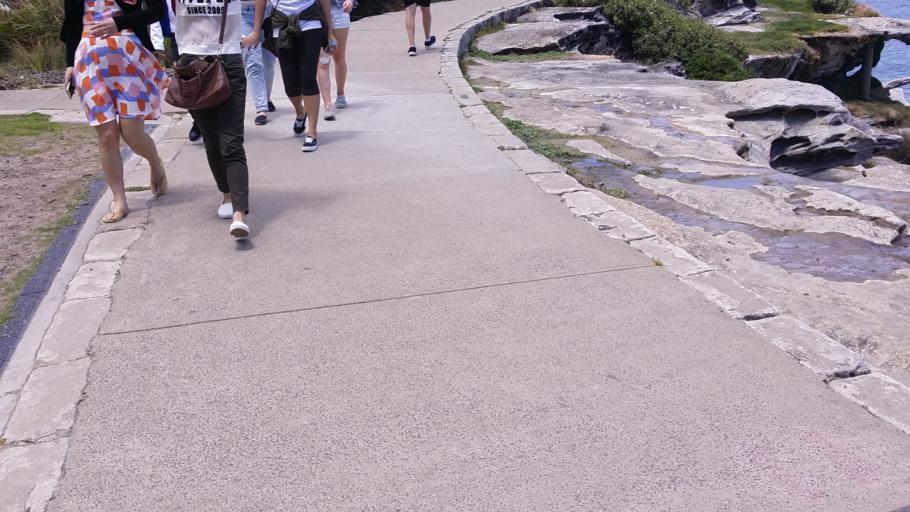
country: AU
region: New South Wales
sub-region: Waverley
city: Bondi Beach
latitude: -33.8988
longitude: 151.2746
